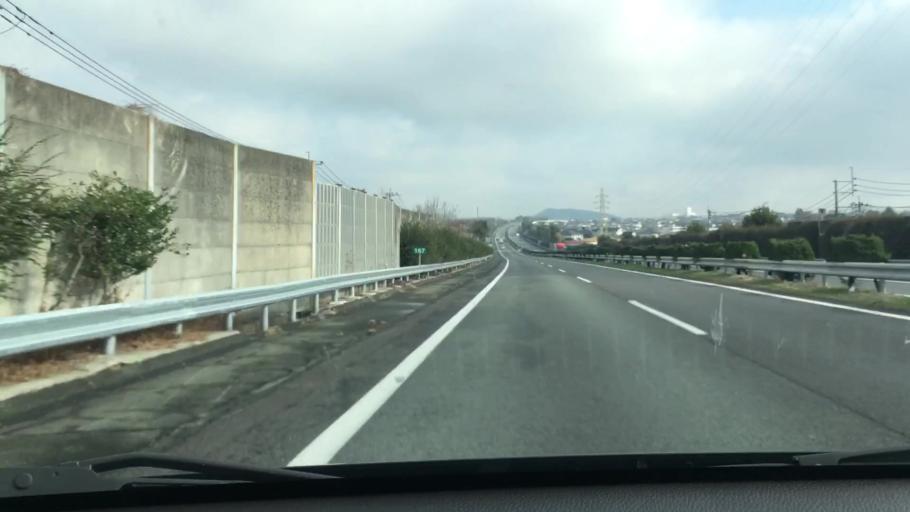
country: JP
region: Kumamoto
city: Ueki
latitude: 32.8599
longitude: 130.7464
